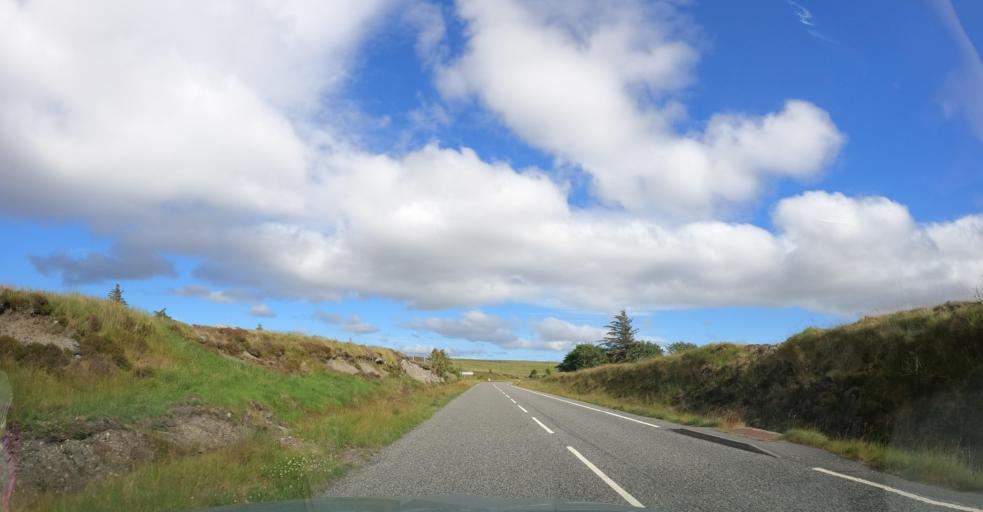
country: GB
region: Scotland
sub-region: Eilean Siar
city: Harris
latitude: 58.1930
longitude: -6.7126
